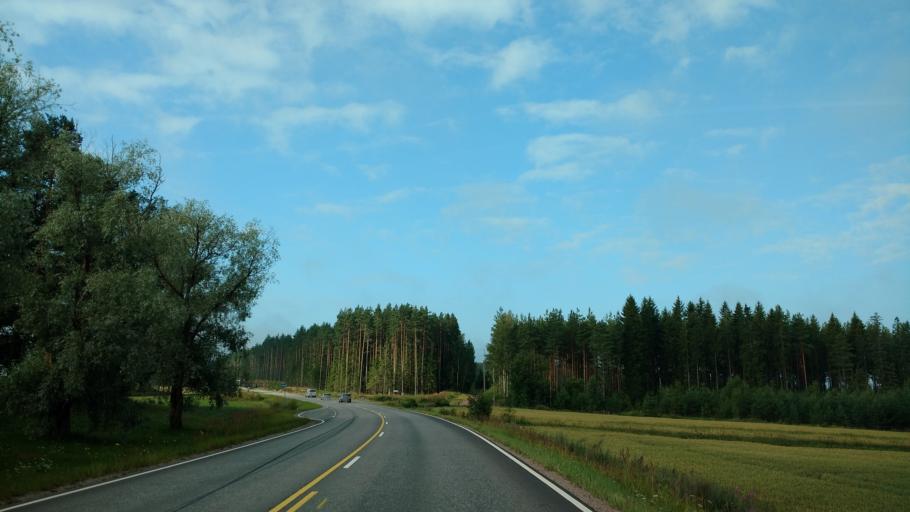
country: FI
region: Varsinais-Suomi
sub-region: Aboland-Turunmaa
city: Vaestanfjaerd
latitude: 60.1270
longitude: 22.6299
